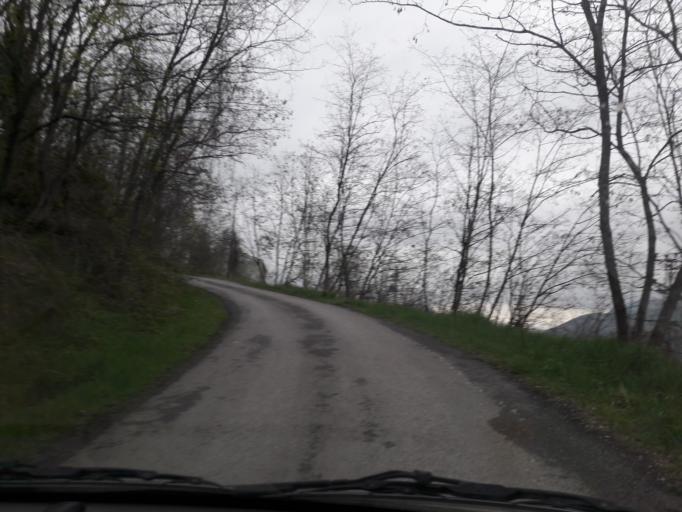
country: TR
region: Trabzon
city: Duzkoy
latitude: 40.9305
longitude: 39.4781
